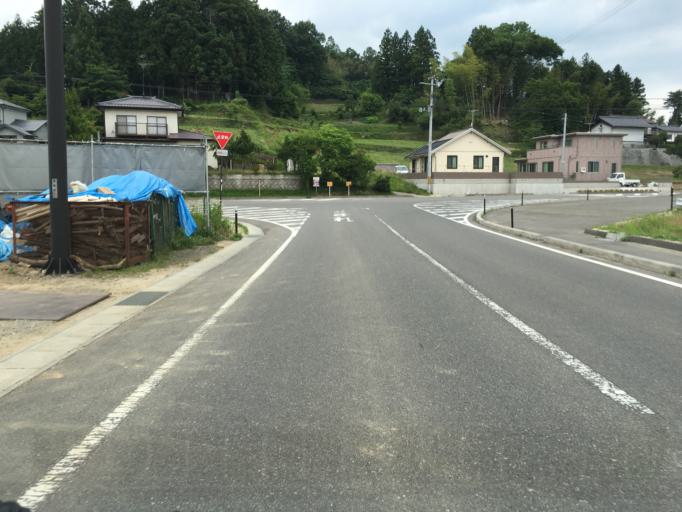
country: JP
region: Fukushima
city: Fukushima-shi
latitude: 37.6524
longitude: 140.5318
